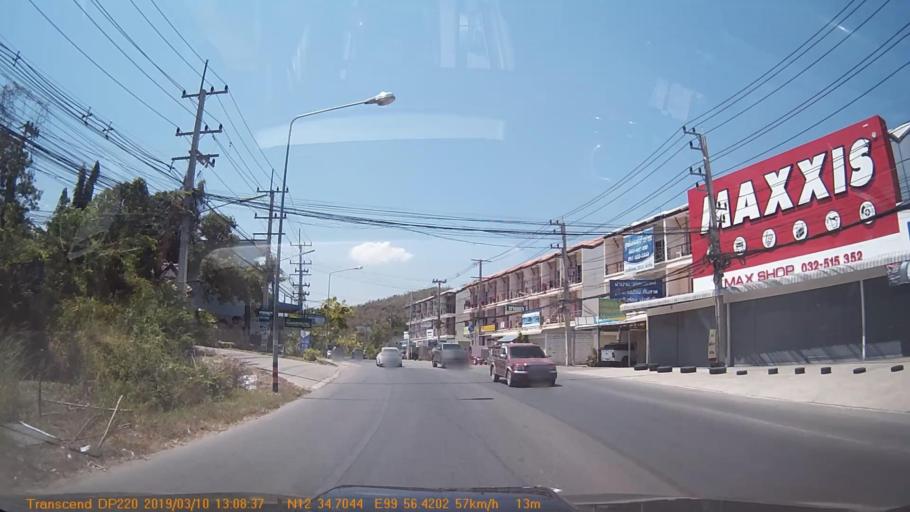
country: TH
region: Prachuap Khiri Khan
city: Hua Hin
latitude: 12.5785
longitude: 99.9402
